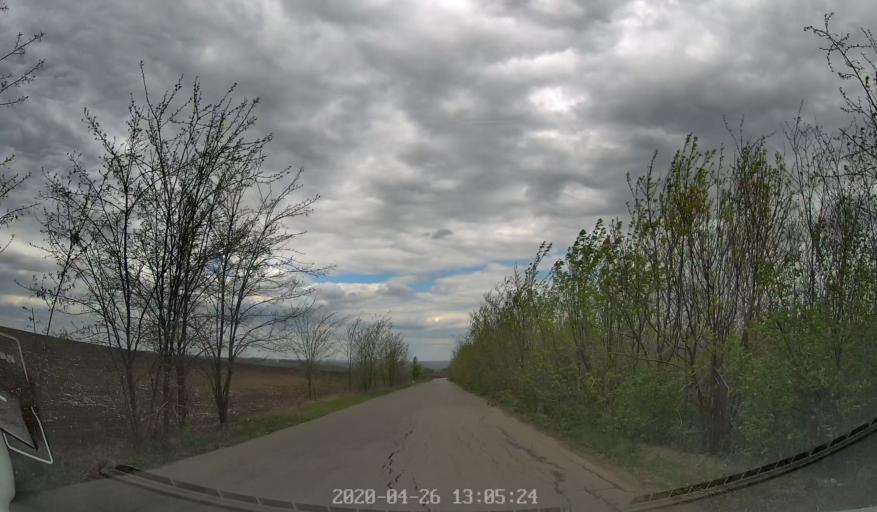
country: MD
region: Chisinau
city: Vadul lui Voda
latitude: 47.0757
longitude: 29.0662
